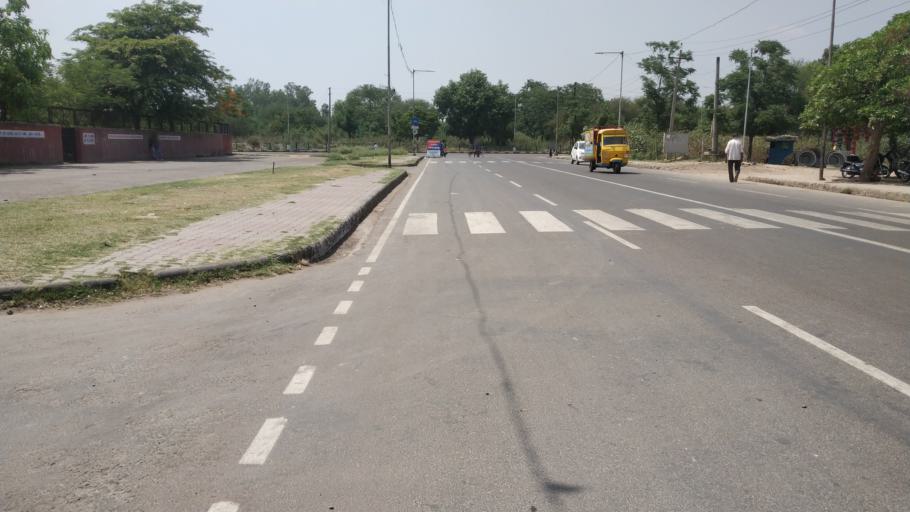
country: IN
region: Punjab
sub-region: Ajitgarh
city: Mohali
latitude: 30.7136
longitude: 76.7328
